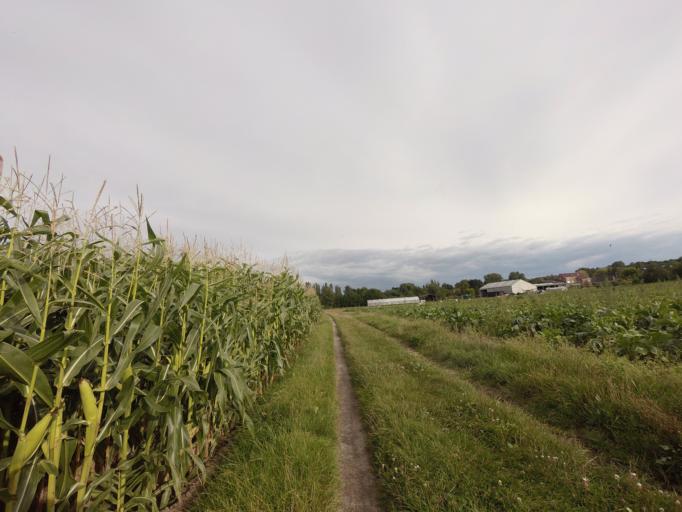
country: BE
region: Flanders
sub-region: Provincie Vlaams-Brabant
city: Boortmeerbeek
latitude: 50.9843
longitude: 4.5392
